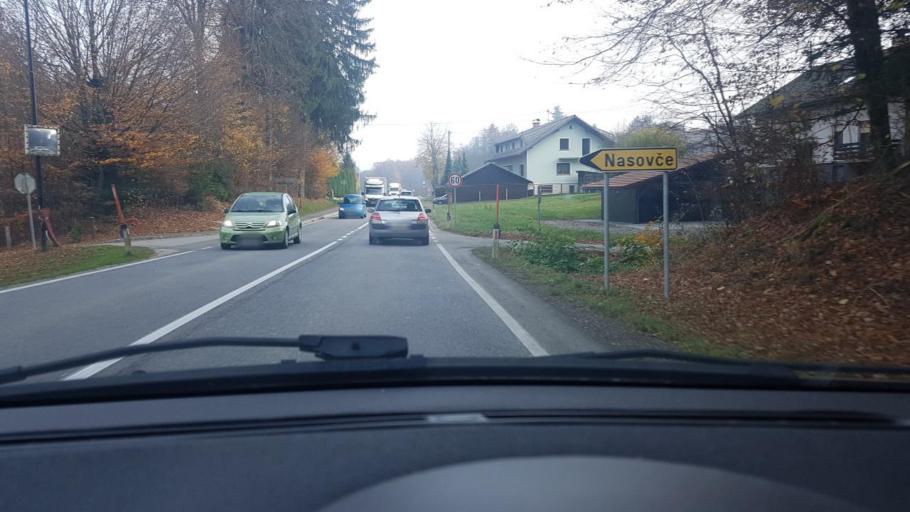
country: SI
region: Komenda
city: Komenda
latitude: 46.2098
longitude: 14.5148
